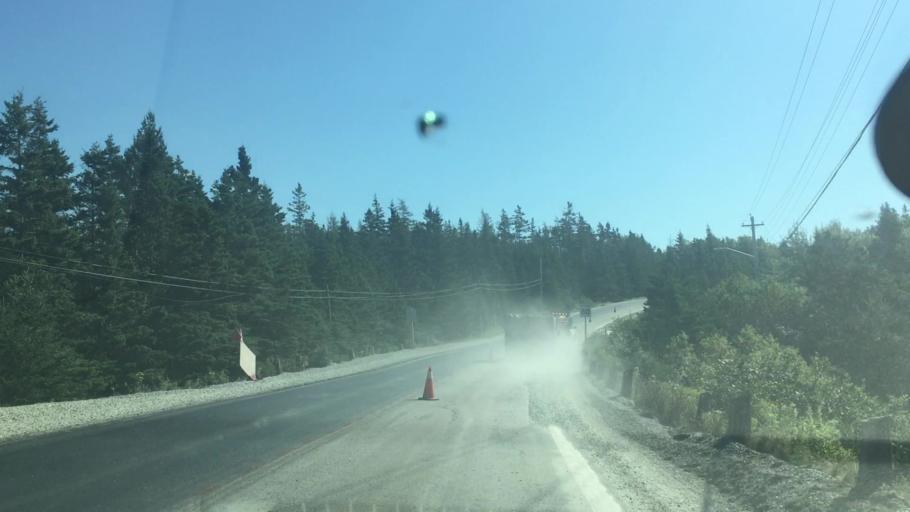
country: CA
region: Nova Scotia
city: New Glasgow
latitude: 44.9069
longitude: -62.4927
